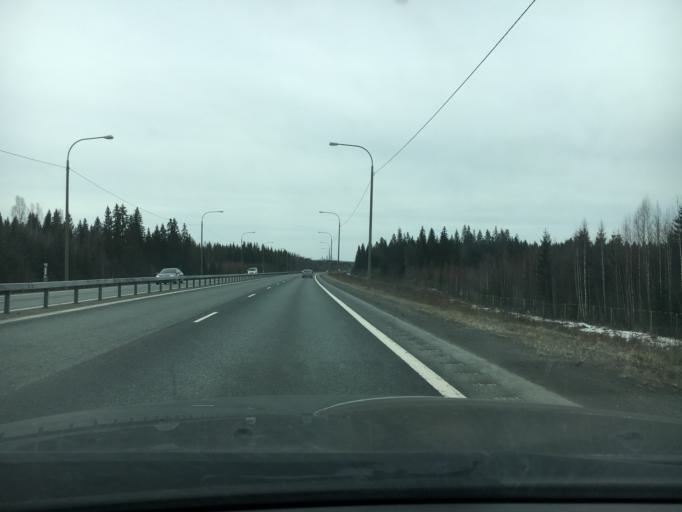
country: FI
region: Northern Savo
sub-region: Kuopio
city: Kuopio
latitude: 62.7659
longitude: 27.5823
